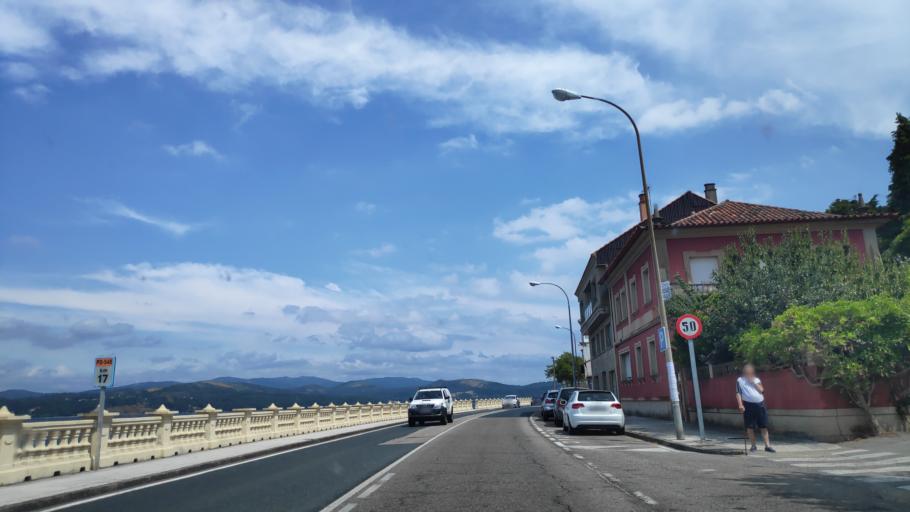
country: ES
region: Galicia
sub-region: Provincia de Pontevedra
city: Vilagarcia de Arousa
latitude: 42.6165
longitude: -8.7758
